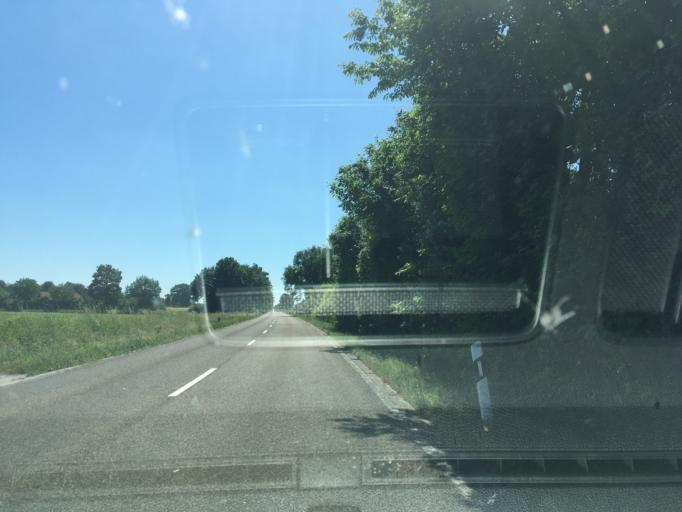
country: DE
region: North Rhine-Westphalia
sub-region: Regierungsbezirk Munster
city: Raesfeld
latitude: 51.7898
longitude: 6.8143
